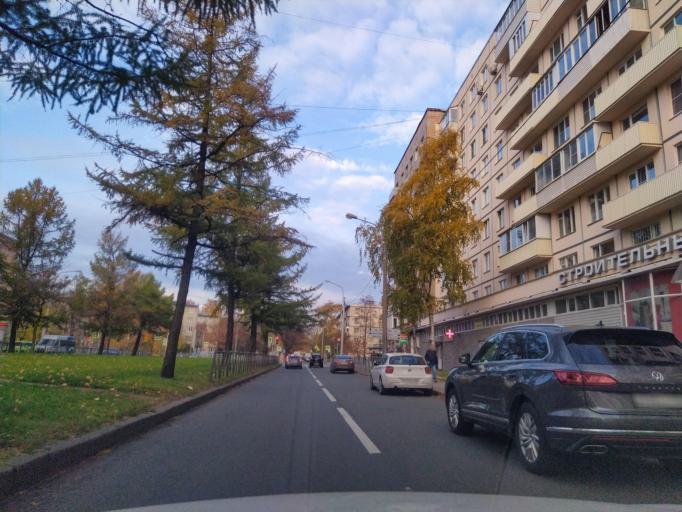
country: RU
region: Leningrad
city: Kalininskiy
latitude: 59.9814
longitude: 30.4079
